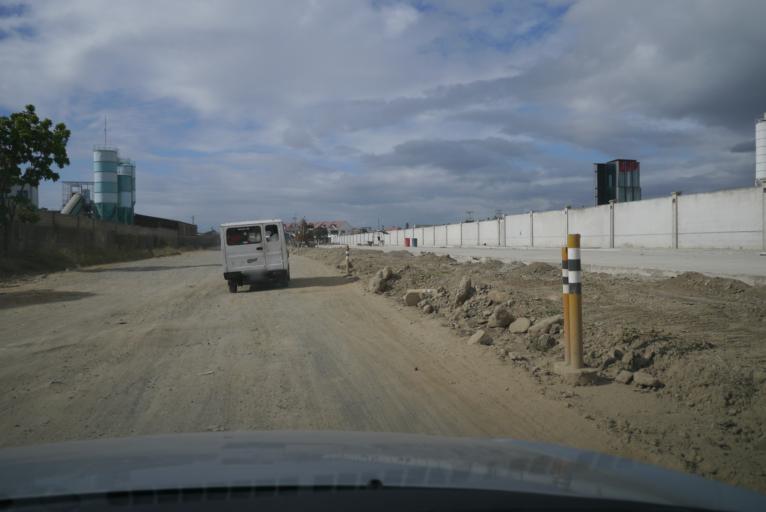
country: PH
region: Calabarzon
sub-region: Province of Rizal
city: Taytay
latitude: 14.5455
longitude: 121.1279
